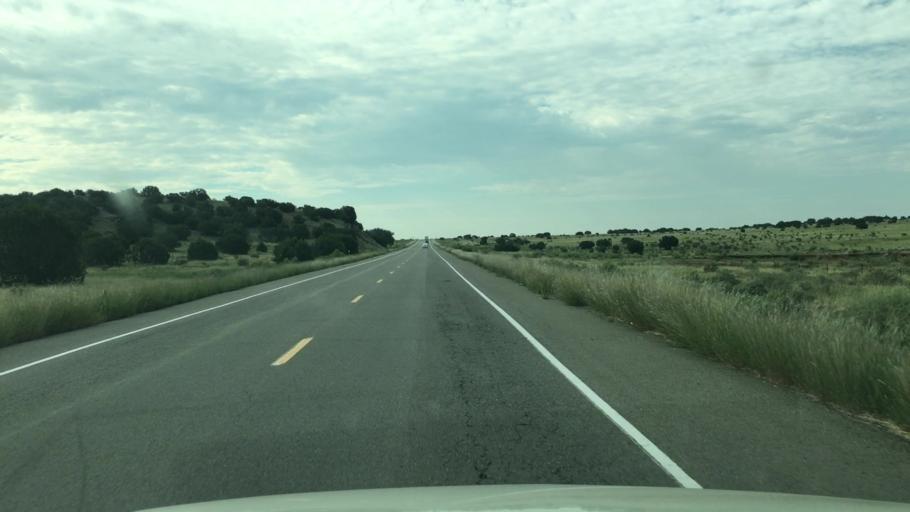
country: US
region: New Mexico
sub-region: Santa Fe County
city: Eldorado at Santa Fe
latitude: 35.4347
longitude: -105.8815
